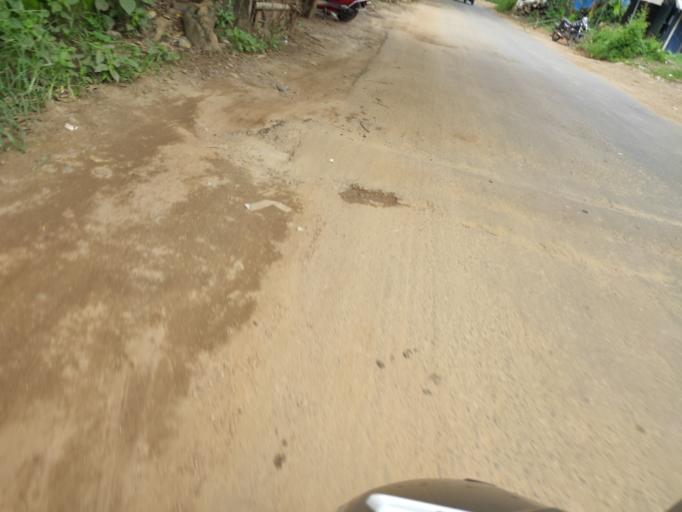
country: IN
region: Kerala
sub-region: Malappuram
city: Manjeri
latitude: 11.2426
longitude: 76.2871
